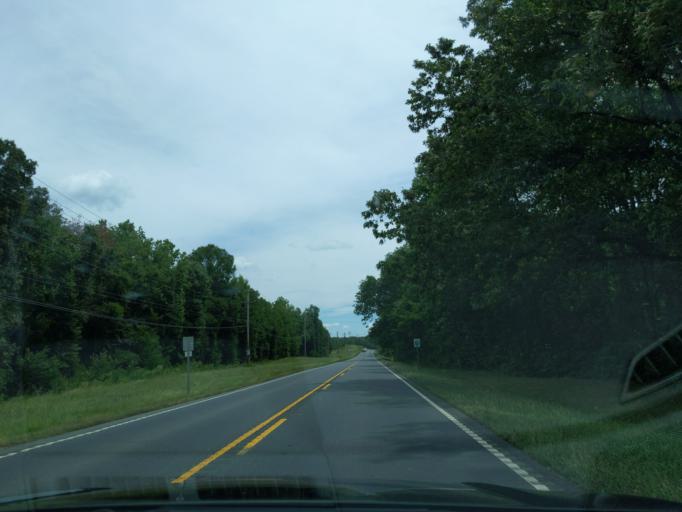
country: US
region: North Carolina
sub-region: Rowan County
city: Rockwell
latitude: 35.4667
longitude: -80.2936
